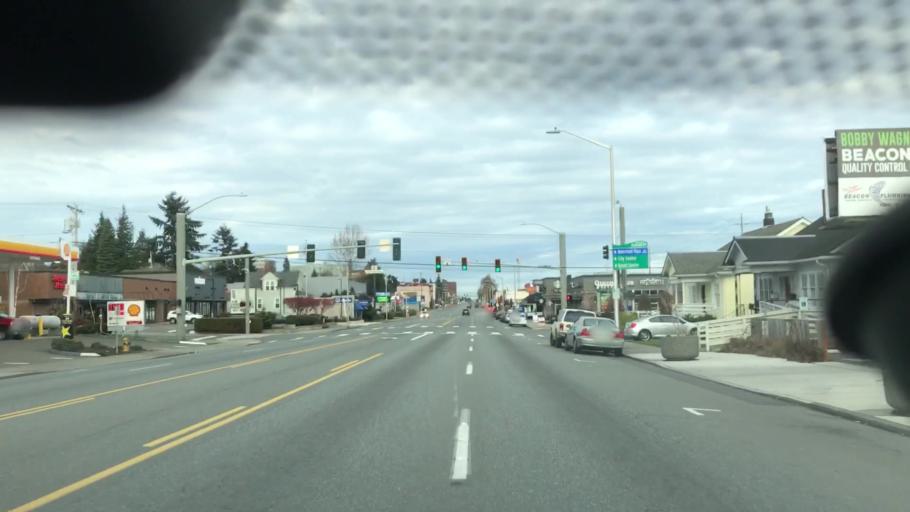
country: US
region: Washington
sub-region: Snohomish County
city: Everett
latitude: 47.9682
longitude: -122.2011
